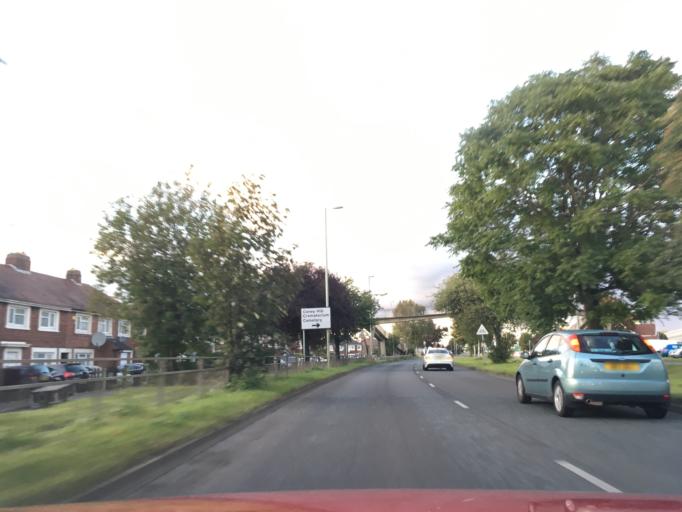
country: GB
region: England
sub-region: Gloucestershire
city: Gloucester
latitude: 51.8527
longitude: -2.2250
